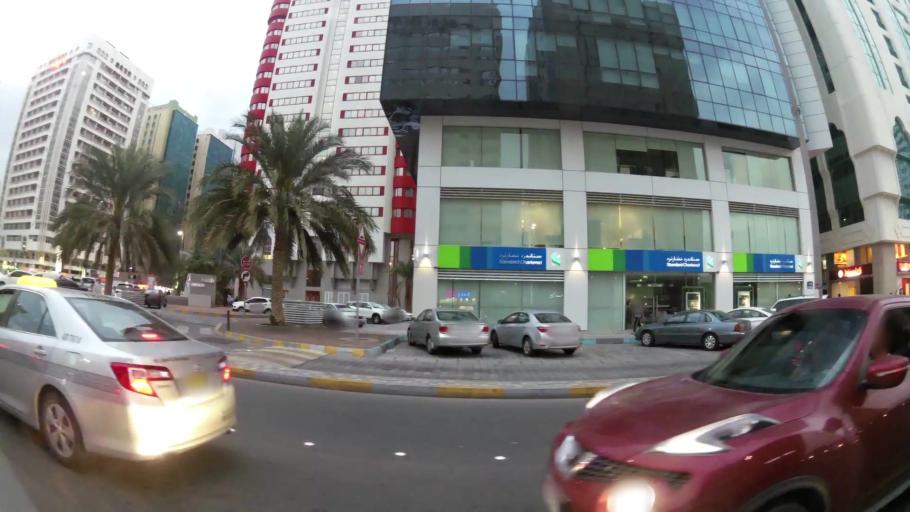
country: AE
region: Abu Dhabi
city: Abu Dhabi
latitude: 24.4901
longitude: 54.3702
